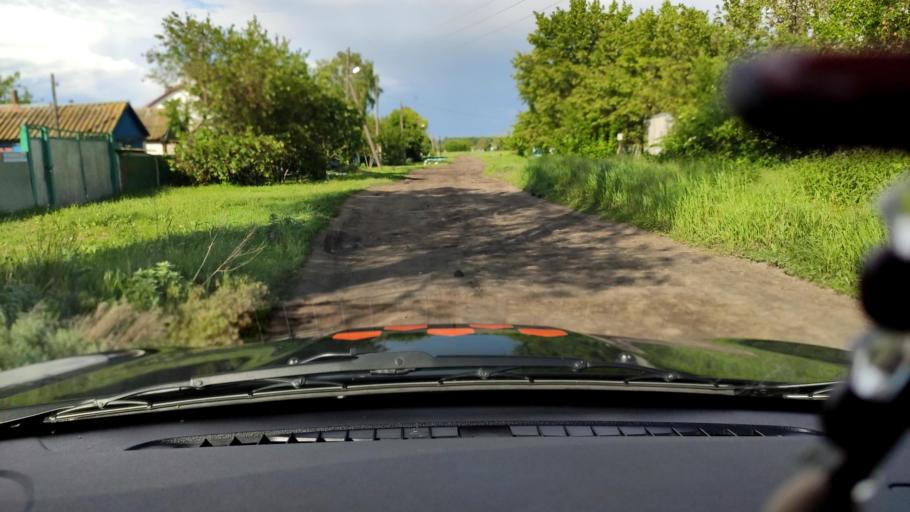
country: RU
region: Voronezj
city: Uryv-Pokrovka
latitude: 51.1147
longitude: 39.1800
